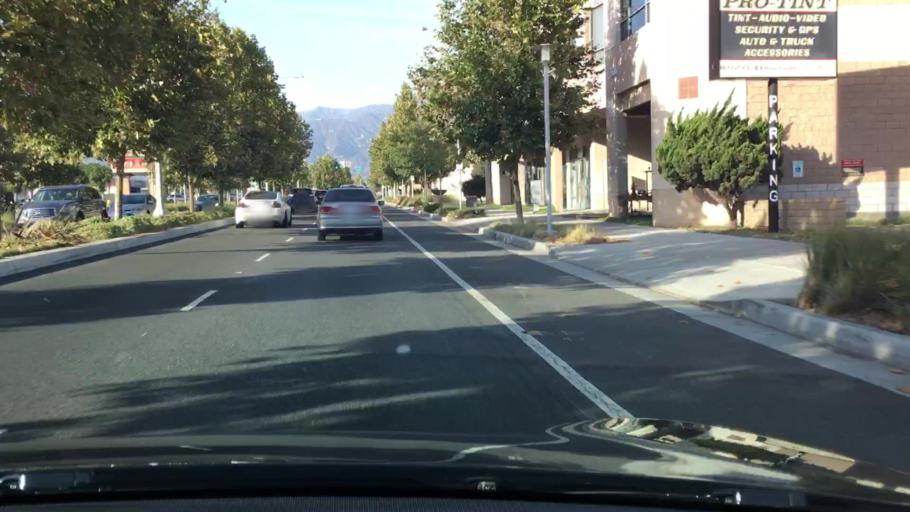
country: US
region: California
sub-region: Los Angeles County
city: Temple City
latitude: 34.0995
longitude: -118.0734
